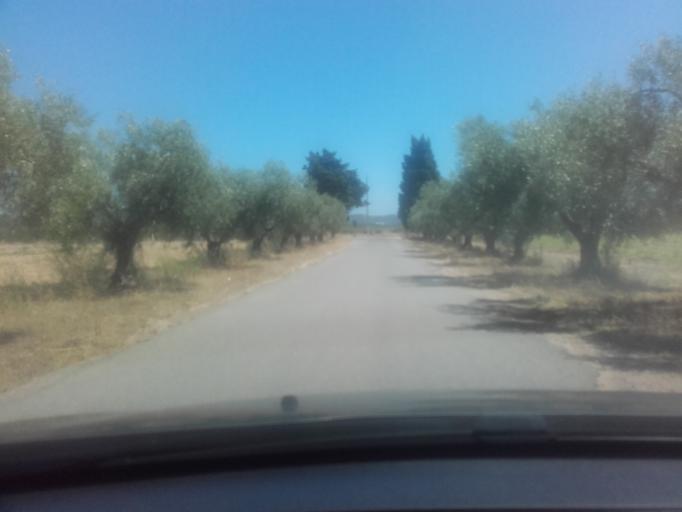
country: ES
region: Catalonia
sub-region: Provincia de Tarragona
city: Santa Oliva
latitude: 41.2514
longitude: 1.5399
